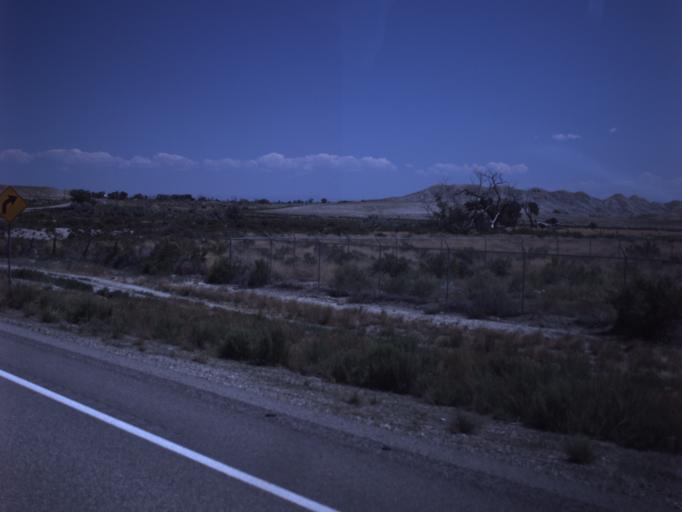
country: US
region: Utah
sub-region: Emery County
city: Ferron
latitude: 39.1135
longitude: -111.1248
